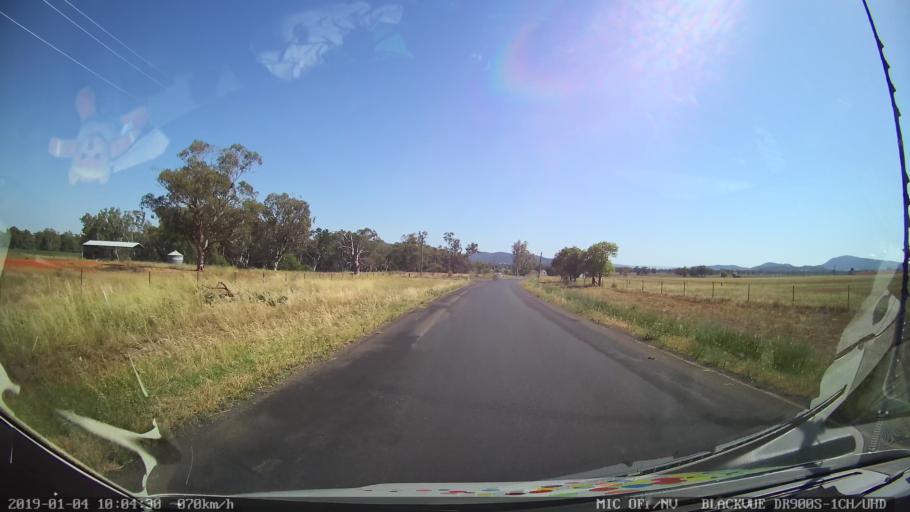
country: AU
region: New South Wales
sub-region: Cabonne
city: Canowindra
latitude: -33.4519
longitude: 148.3612
